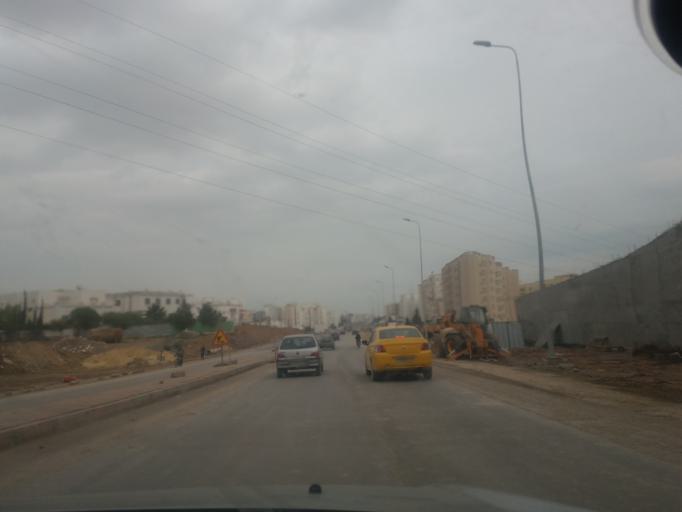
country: TN
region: Tunis
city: Tunis
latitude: 36.8556
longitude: 10.1473
